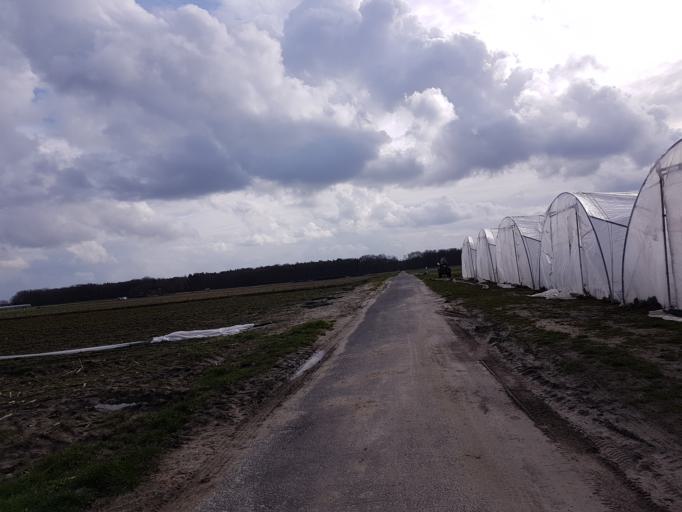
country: DE
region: North Rhine-Westphalia
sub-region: Regierungsbezirk Dusseldorf
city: Bruggen
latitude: 51.2569
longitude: 6.1932
